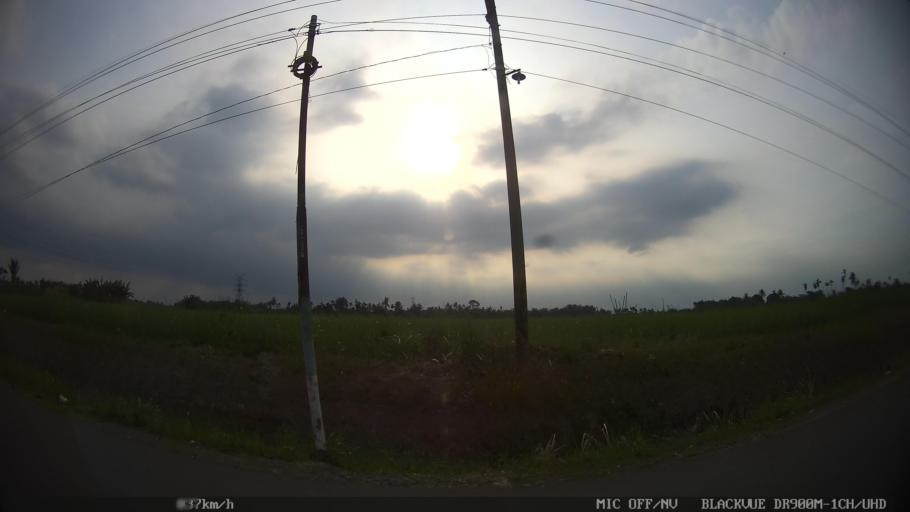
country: ID
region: North Sumatra
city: Sunggal
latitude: 3.5850
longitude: 98.5516
